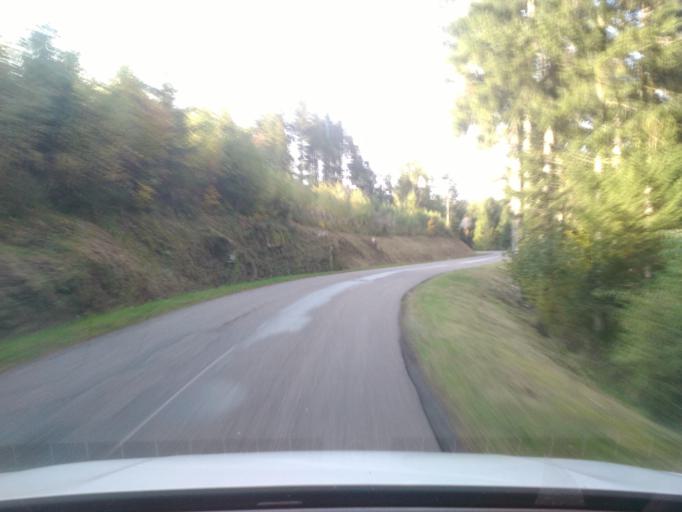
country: FR
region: Lorraine
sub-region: Departement des Vosges
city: Sainte-Marguerite
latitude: 48.3209
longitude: 7.0327
